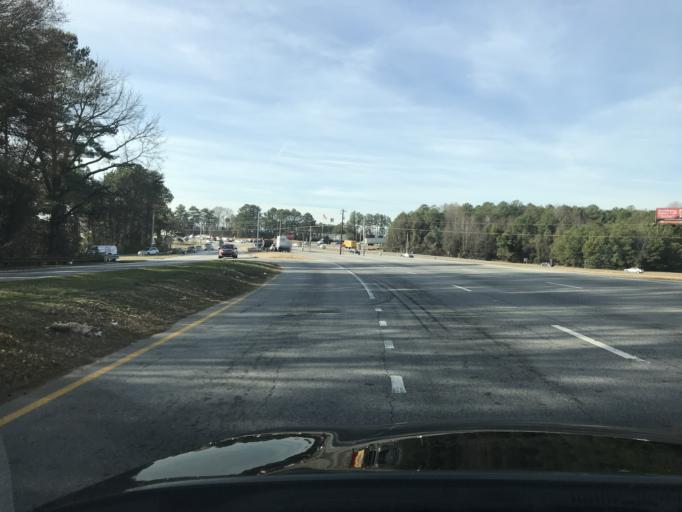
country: US
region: Georgia
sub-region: Clayton County
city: Forest Park
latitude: 33.6168
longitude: -84.4007
